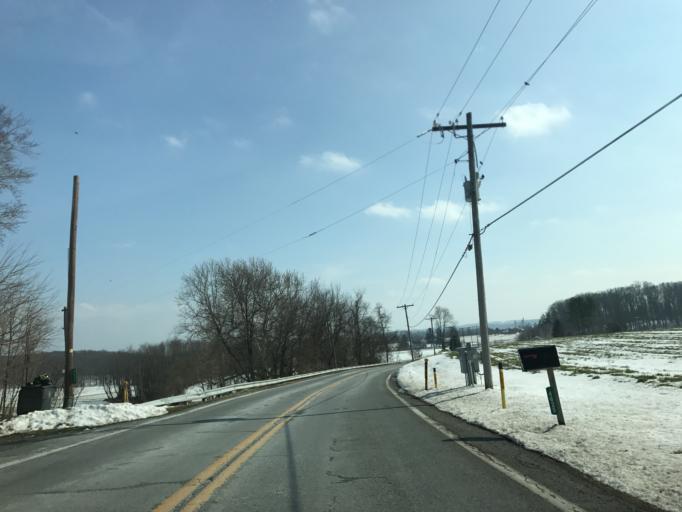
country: US
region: Pennsylvania
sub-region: York County
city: Susquehanna Trails
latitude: 39.7148
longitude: -76.3888
